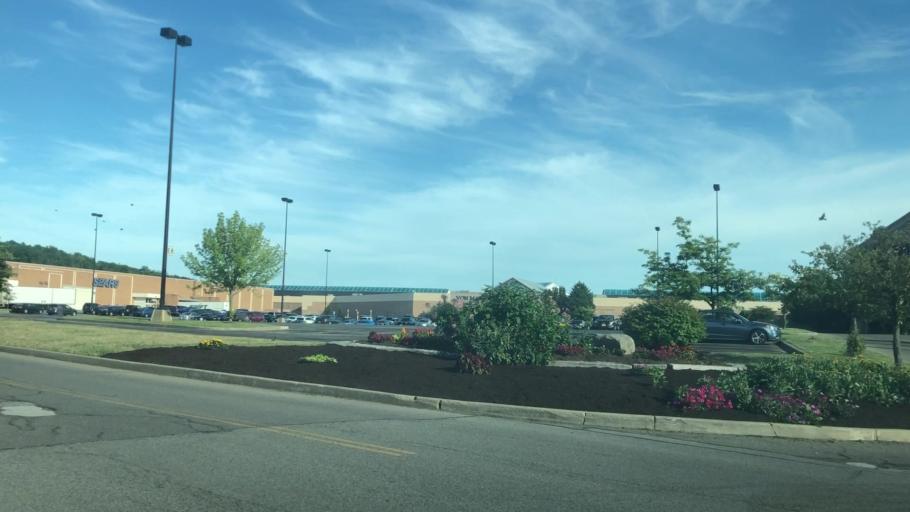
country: US
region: New York
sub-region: Ontario County
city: Victor
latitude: 43.0317
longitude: -77.4465
